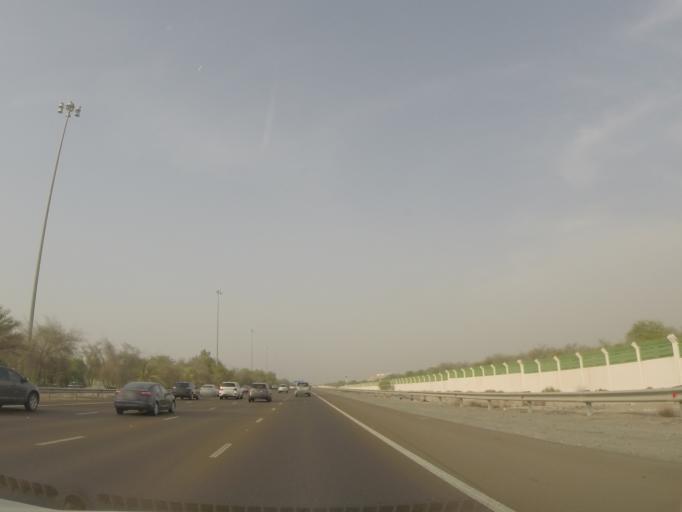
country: AE
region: Dubai
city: Dubai
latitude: 24.7188
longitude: 54.8052
